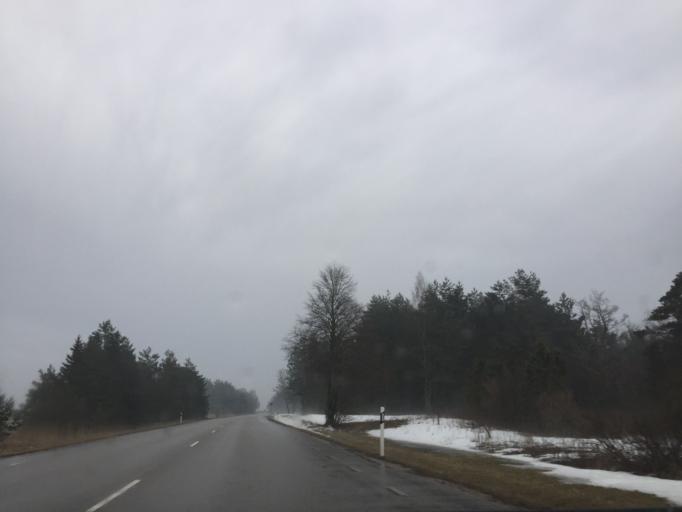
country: EE
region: Saare
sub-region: Orissaare vald
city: Orissaare
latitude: 58.5514
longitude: 23.1138
